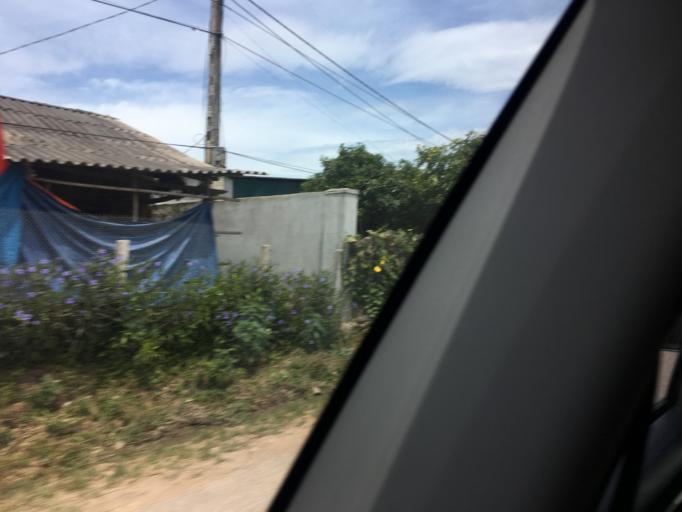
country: VN
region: Ha Tinh
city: Huong Khe
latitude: 18.2634
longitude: 105.6487
